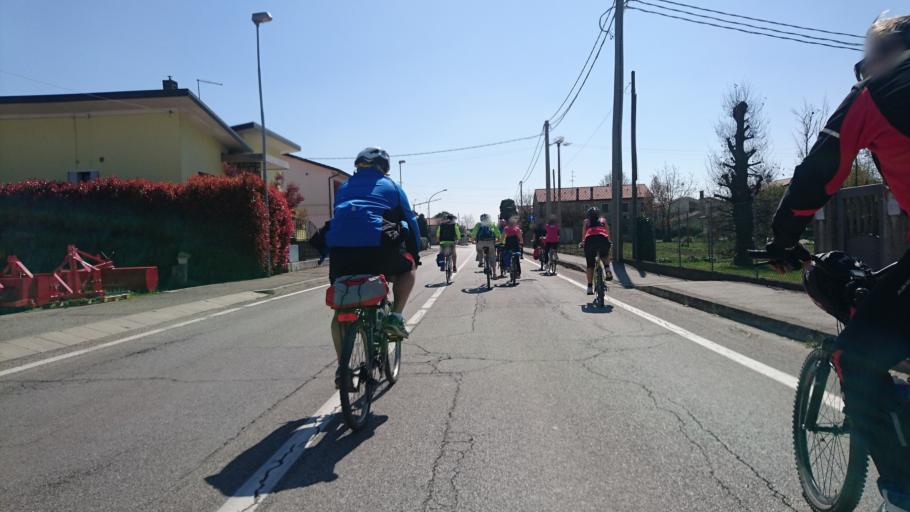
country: IT
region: Veneto
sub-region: Provincia di Padova
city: Piazzola sul Brenta
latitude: 45.5378
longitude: 11.7806
